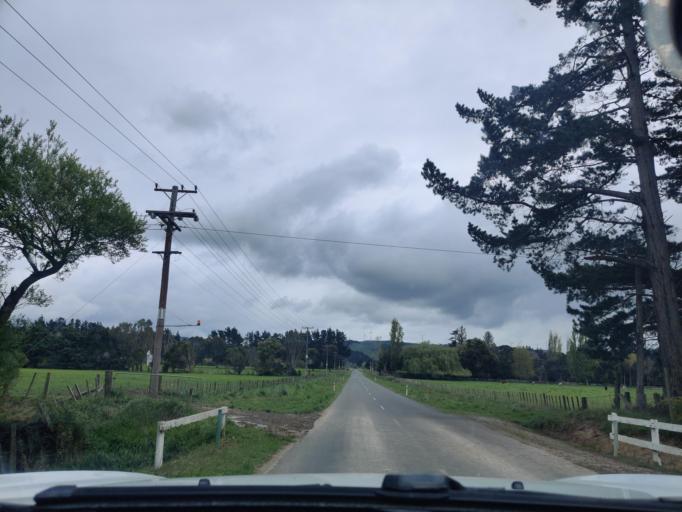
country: NZ
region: Manawatu-Wanganui
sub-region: Palmerston North City
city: Palmerston North
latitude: -40.3204
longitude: 175.8694
